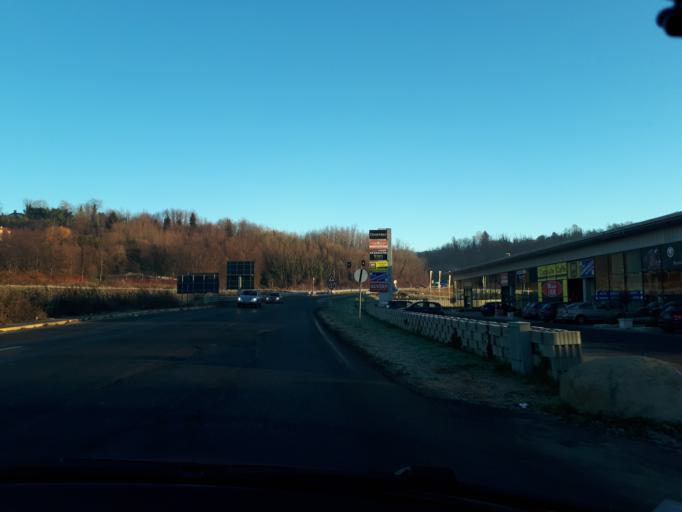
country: IT
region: Lombardy
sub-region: Provincia di Como
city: Grandate
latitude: 45.7705
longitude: 9.0613
